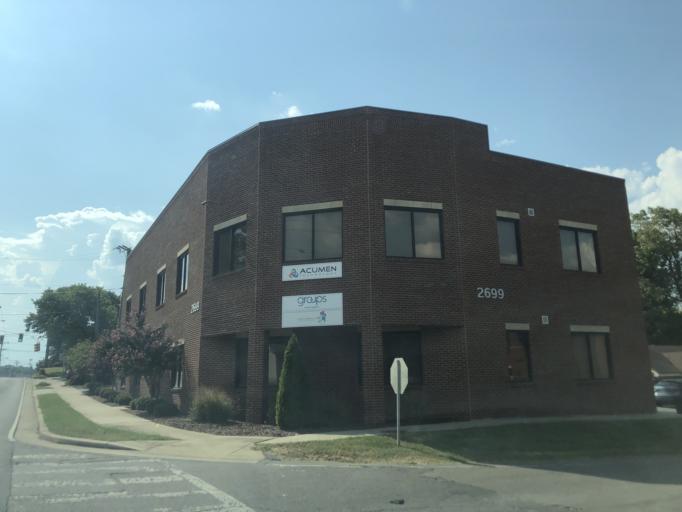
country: US
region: Tennessee
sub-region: Davidson County
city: Oak Hill
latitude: 36.1204
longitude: -86.7678
